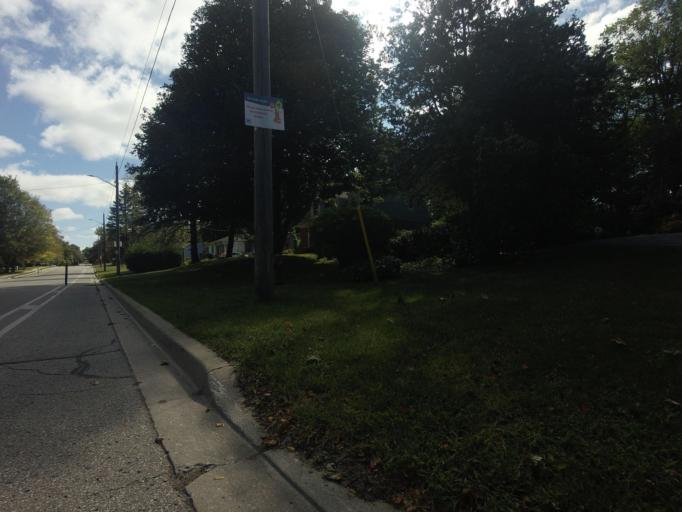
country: CA
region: Ontario
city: Newmarket
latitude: 44.0519
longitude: -79.4705
